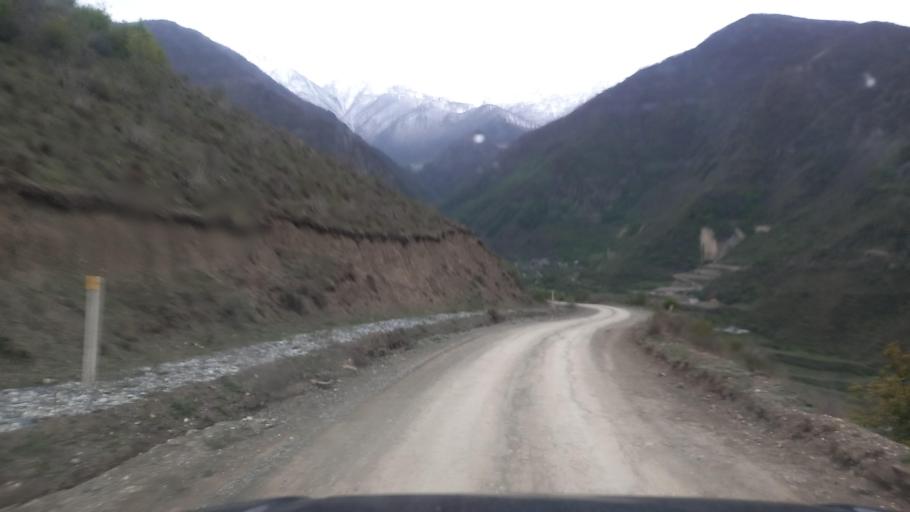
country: RU
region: North Ossetia
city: Mizur
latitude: 42.8594
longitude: 44.1579
